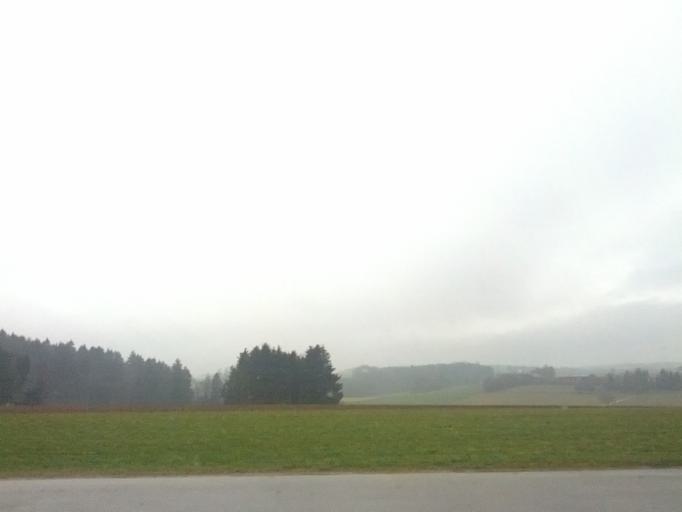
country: DE
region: Baden-Wuerttemberg
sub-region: Tuebingen Region
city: Steinhausen an der Rottum
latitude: 47.9917
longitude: 9.9897
